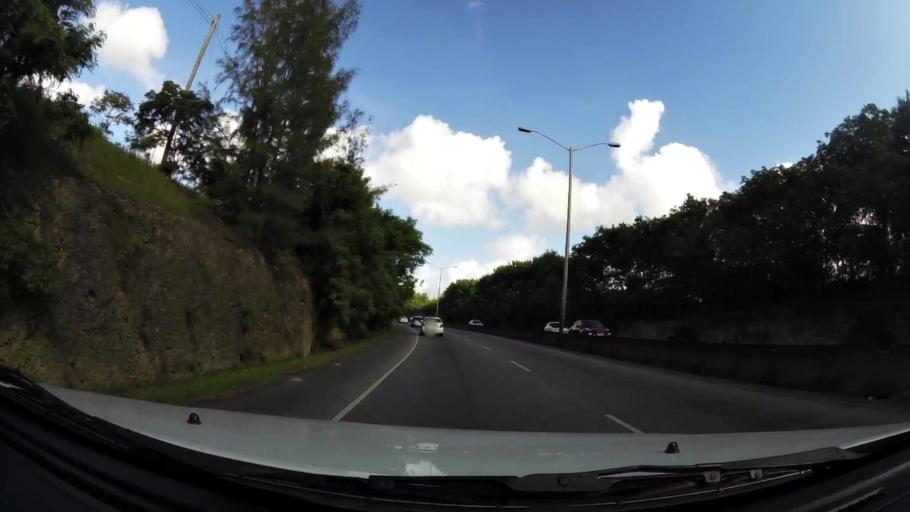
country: BB
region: Saint Michael
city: Bridgetown
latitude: 13.1371
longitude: -59.5998
